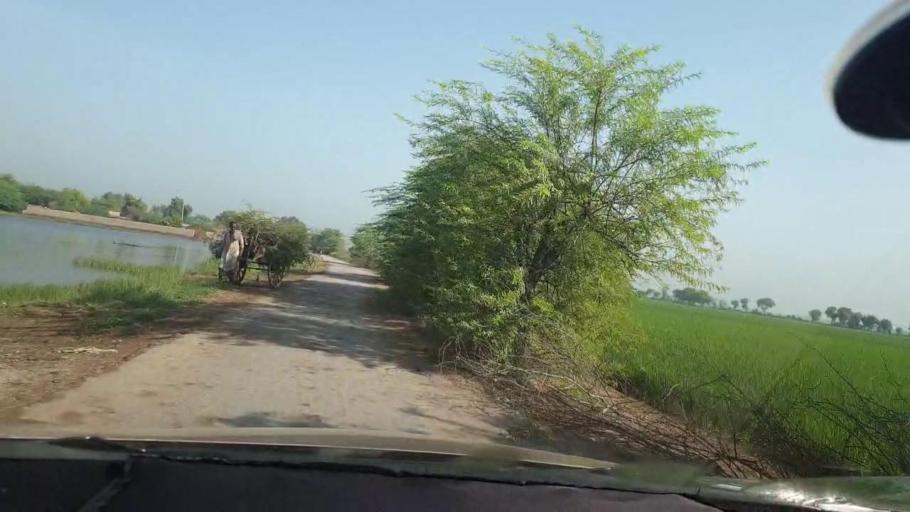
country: PK
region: Sindh
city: Kambar
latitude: 27.6655
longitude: 68.0125
